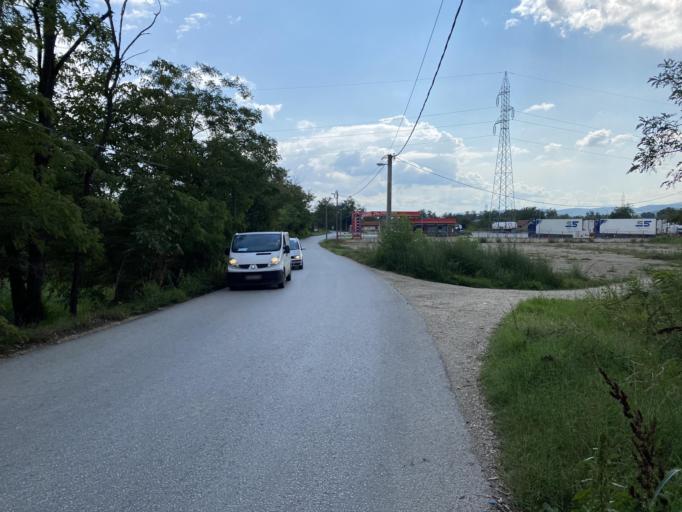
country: MK
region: Kisela Voda
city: Kisela Voda
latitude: 41.9640
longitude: 21.5001
